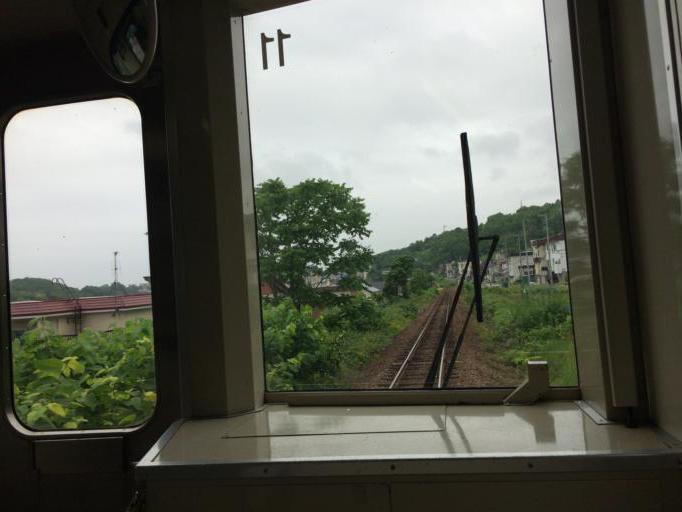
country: JP
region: Hokkaido
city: Otaru
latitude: 43.2096
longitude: 140.9662
